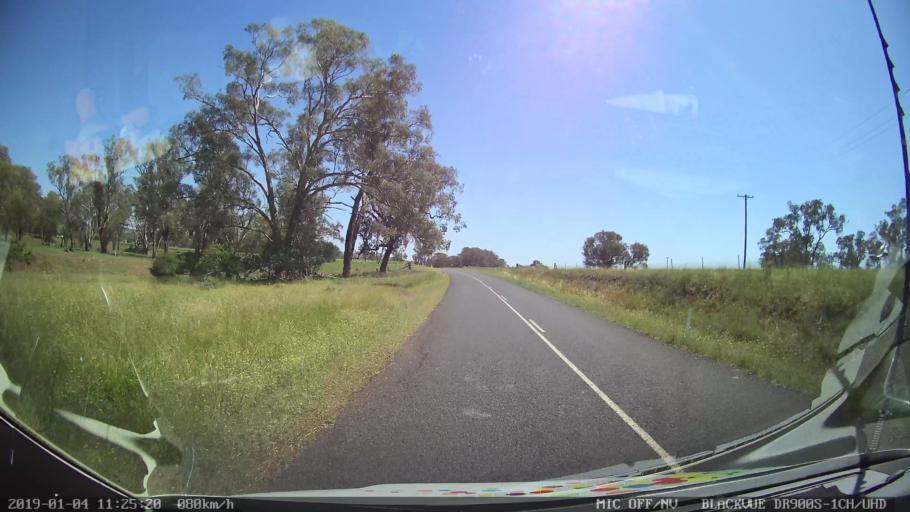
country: AU
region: New South Wales
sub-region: Cabonne
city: Molong
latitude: -33.1261
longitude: 148.7523
